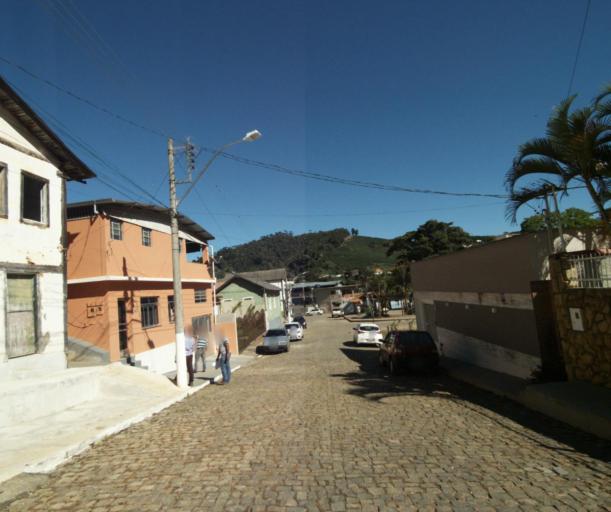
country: BR
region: Minas Gerais
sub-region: Espera Feliz
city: Espera Feliz
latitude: -20.6904
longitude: -41.8459
